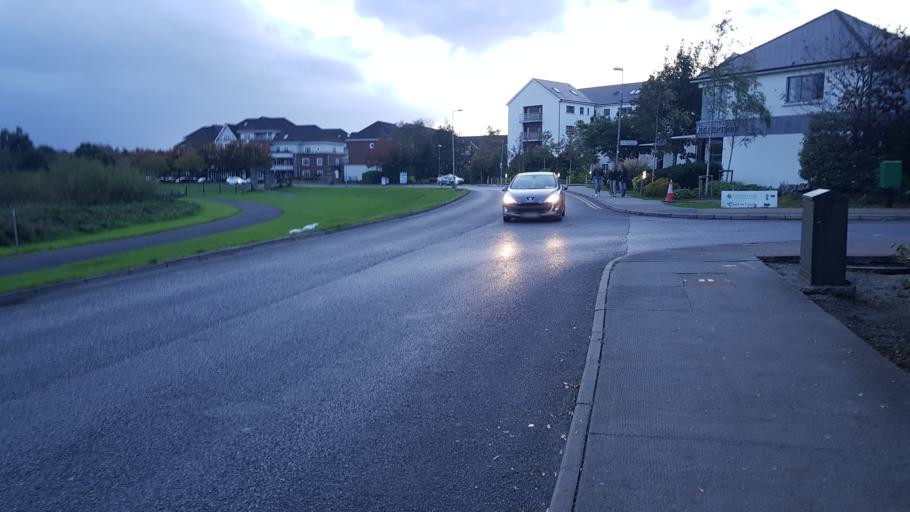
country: IE
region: Connaught
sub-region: County Galway
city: Gaillimh
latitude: 53.2841
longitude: -9.0485
